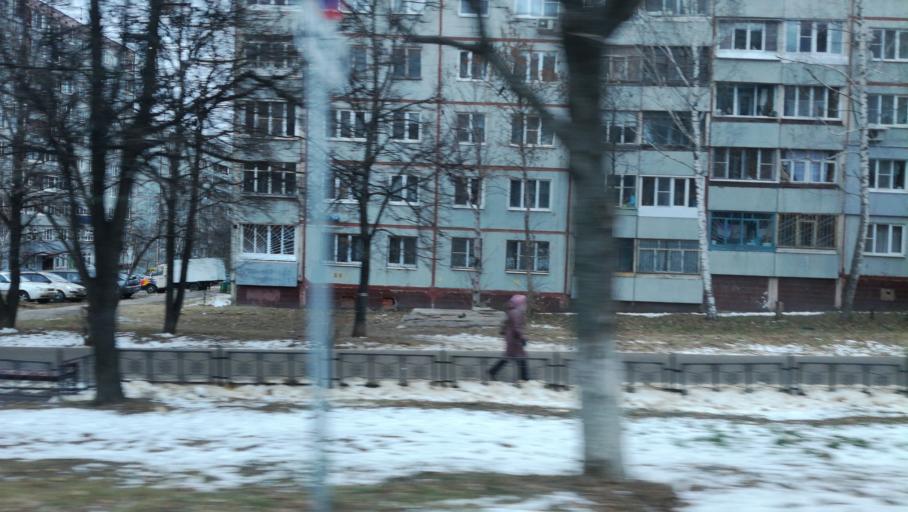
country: RU
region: Tula
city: Tula
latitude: 54.1937
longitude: 37.5916
